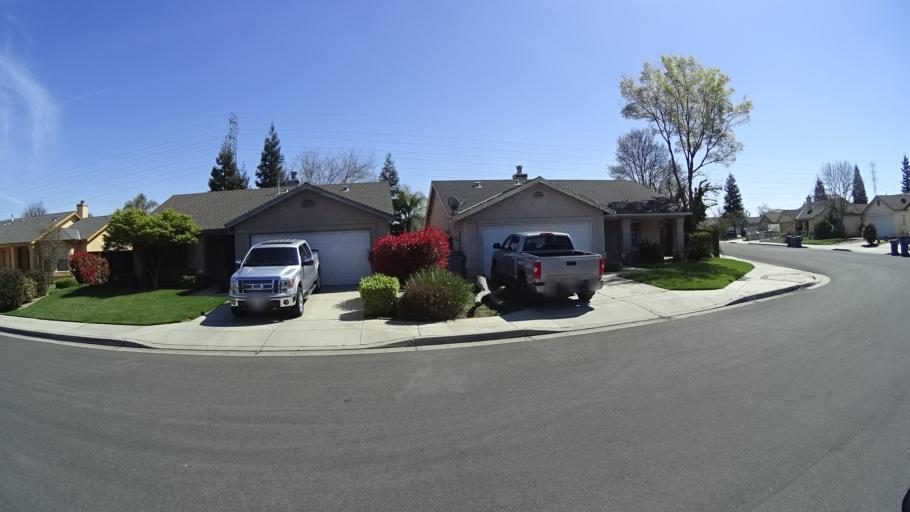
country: US
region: California
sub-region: Fresno County
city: Biola
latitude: 36.8130
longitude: -119.9022
